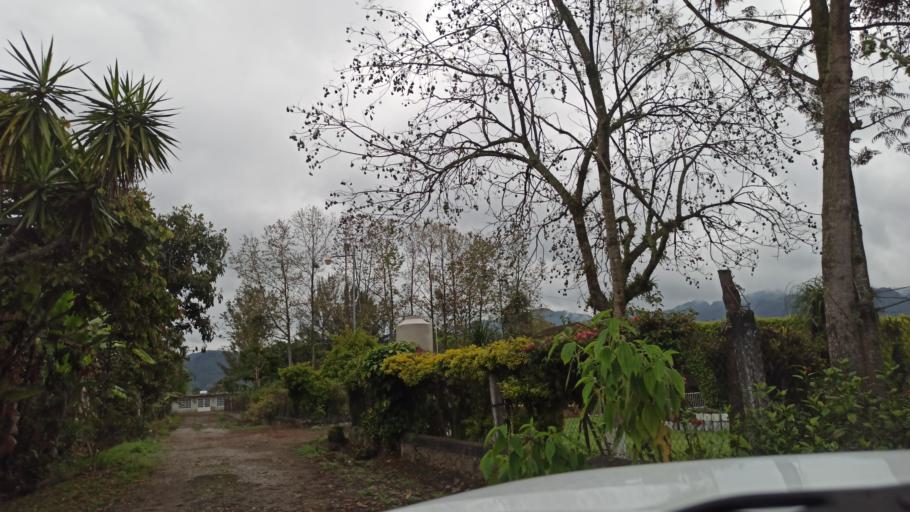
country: MX
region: Veracruz
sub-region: Chocaman
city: San Jose Neria
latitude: 18.9941
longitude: -96.9990
